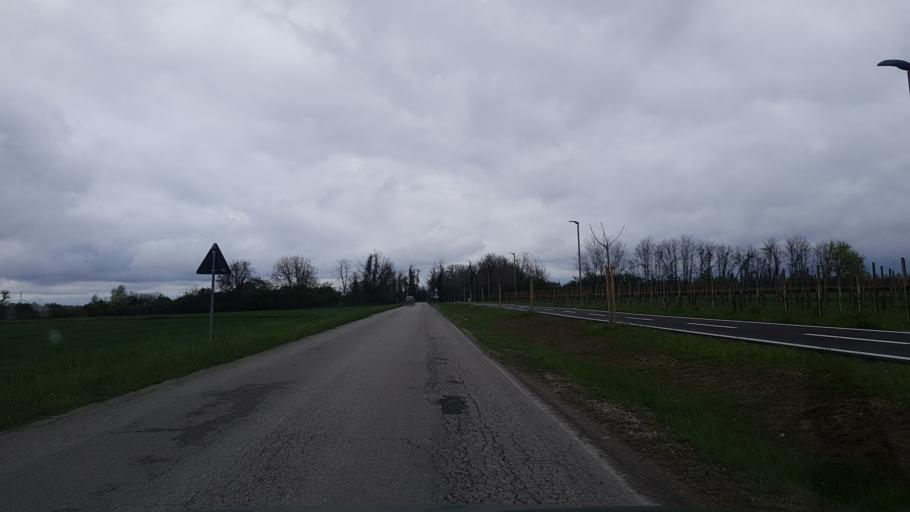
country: IT
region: Friuli Venezia Giulia
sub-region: Provincia di Gorizia
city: Turriaco
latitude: 45.8302
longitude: 13.4435
